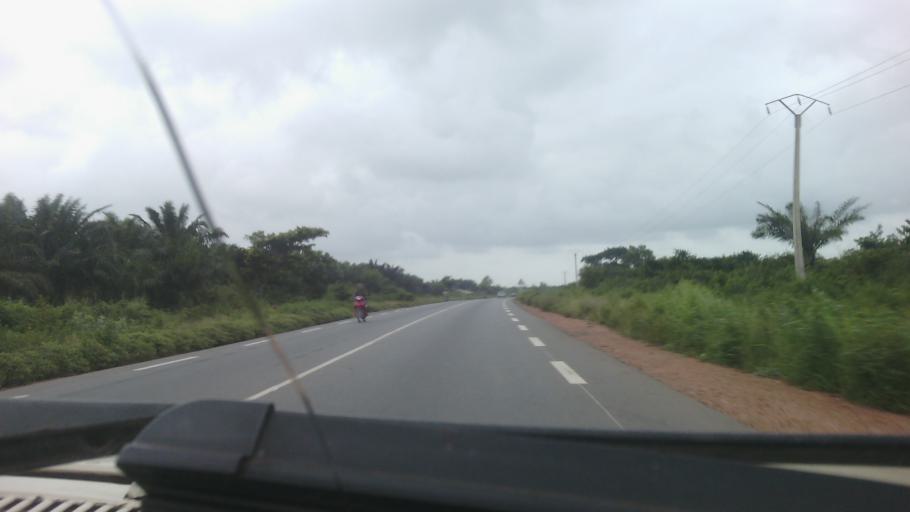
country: BJ
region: Atlantique
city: Ouidah
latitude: 6.3856
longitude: 2.0124
